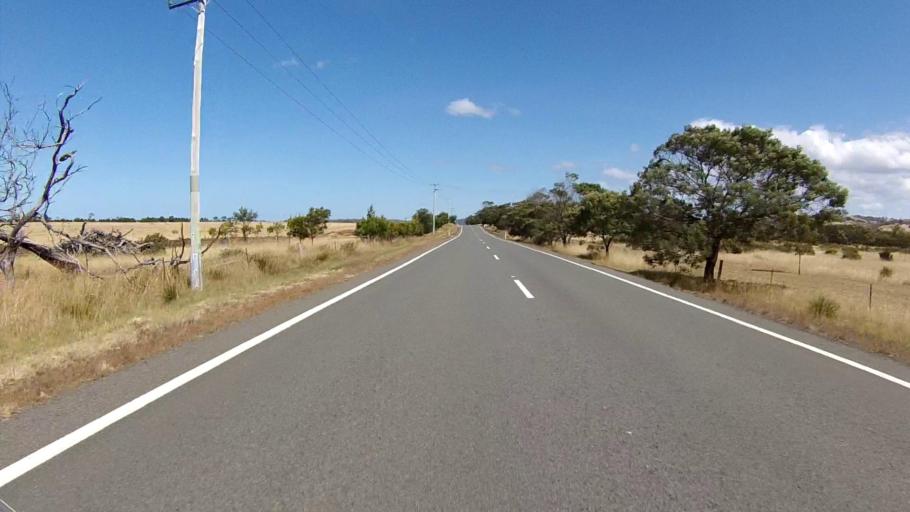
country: AU
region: Tasmania
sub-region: Break O'Day
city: St Helens
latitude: -42.0924
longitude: 148.0655
